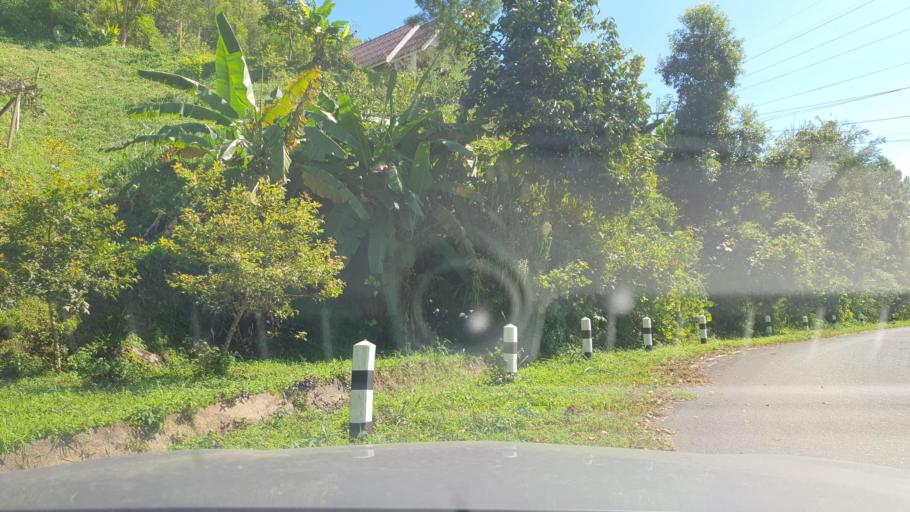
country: TH
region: Chiang Mai
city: Phrao
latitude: 19.3325
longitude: 99.3141
